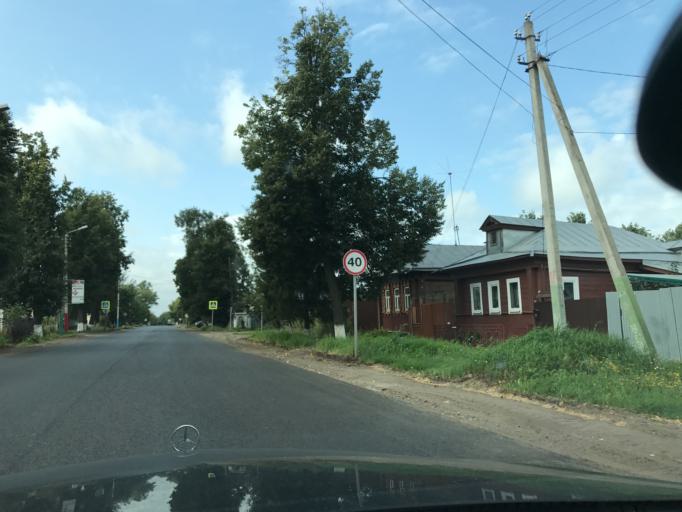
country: RU
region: Nizjnij Novgorod
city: Taremskoye
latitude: 55.9579
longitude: 43.0488
